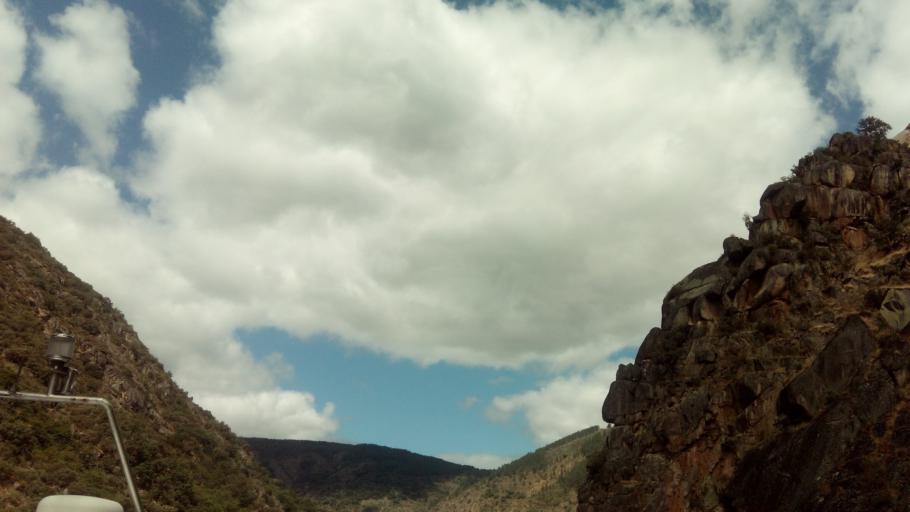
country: ES
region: Galicia
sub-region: Provincia de Lugo
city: Lobios
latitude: 42.3942
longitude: -7.5584
